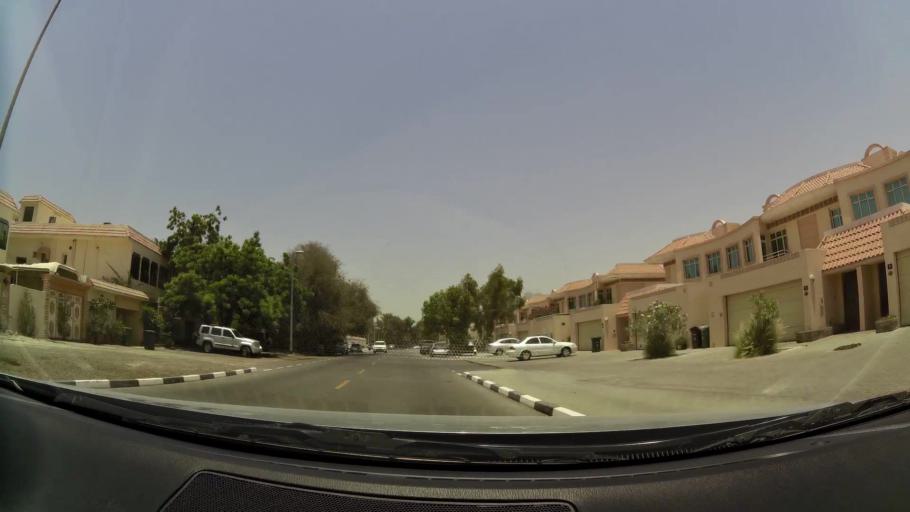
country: AE
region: Dubai
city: Dubai
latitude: 25.1727
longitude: 55.2390
